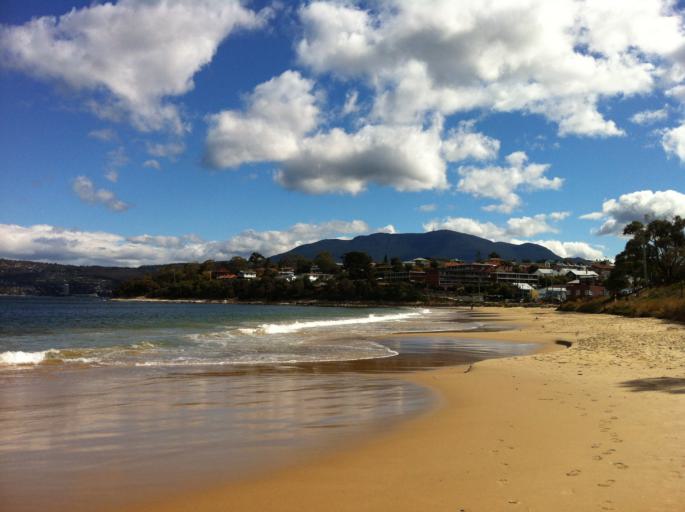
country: AU
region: Tasmania
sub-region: Clarence
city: Bellerive
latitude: -42.8789
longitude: 147.3741
